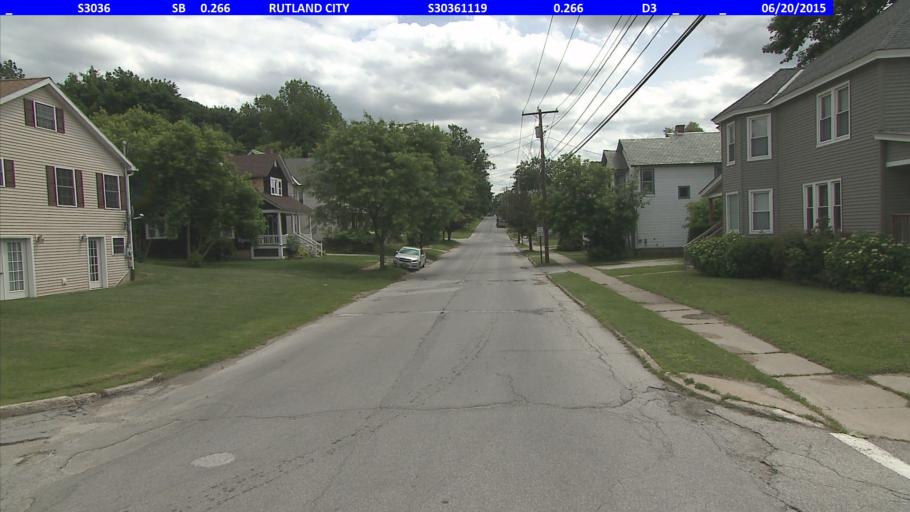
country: US
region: Vermont
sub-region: Rutland County
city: Rutland
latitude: 43.6122
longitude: -72.9763
